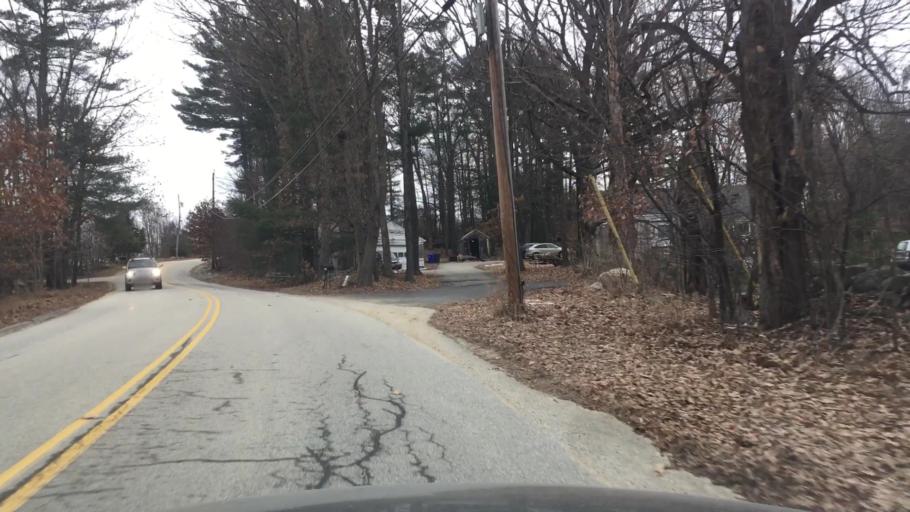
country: US
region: New Hampshire
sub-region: Hillsborough County
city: Mont Vernon
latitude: 42.9216
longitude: -71.6013
